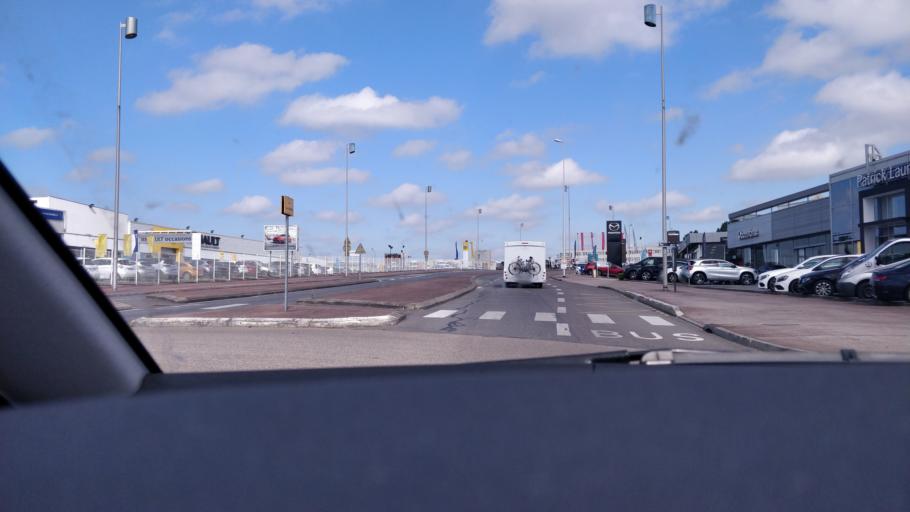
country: FR
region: Limousin
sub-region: Departement de la Haute-Vienne
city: Couzeix
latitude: 45.8673
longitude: 1.2695
